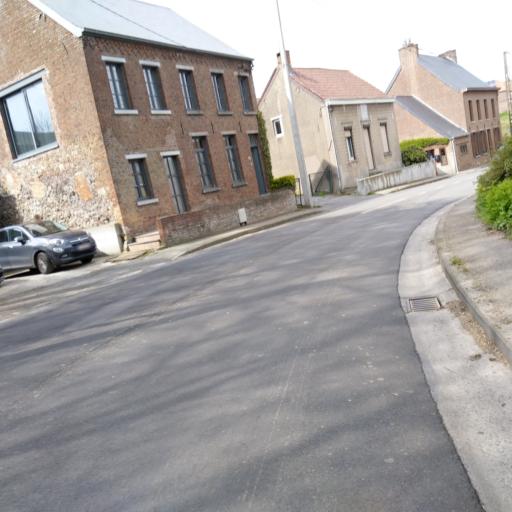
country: BE
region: Wallonia
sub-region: Province du Hainaut
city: Quevy-le-Petit
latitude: 50.3715
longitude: 3.9257
